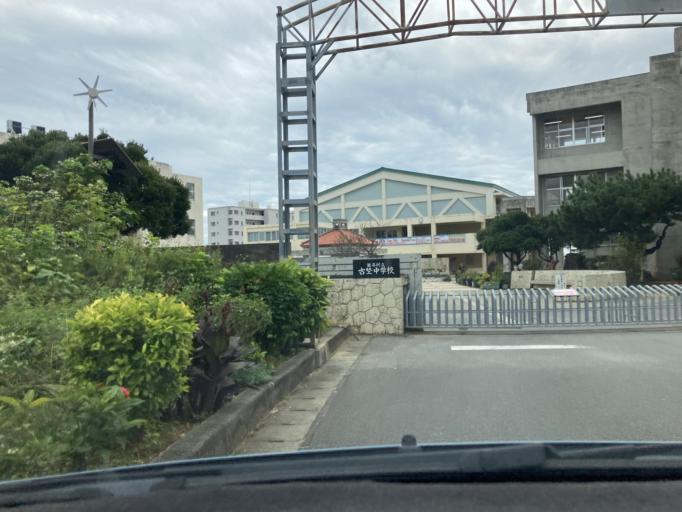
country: JP
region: Okinawa
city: Okinawa
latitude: 26.3814
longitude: 127.7526
